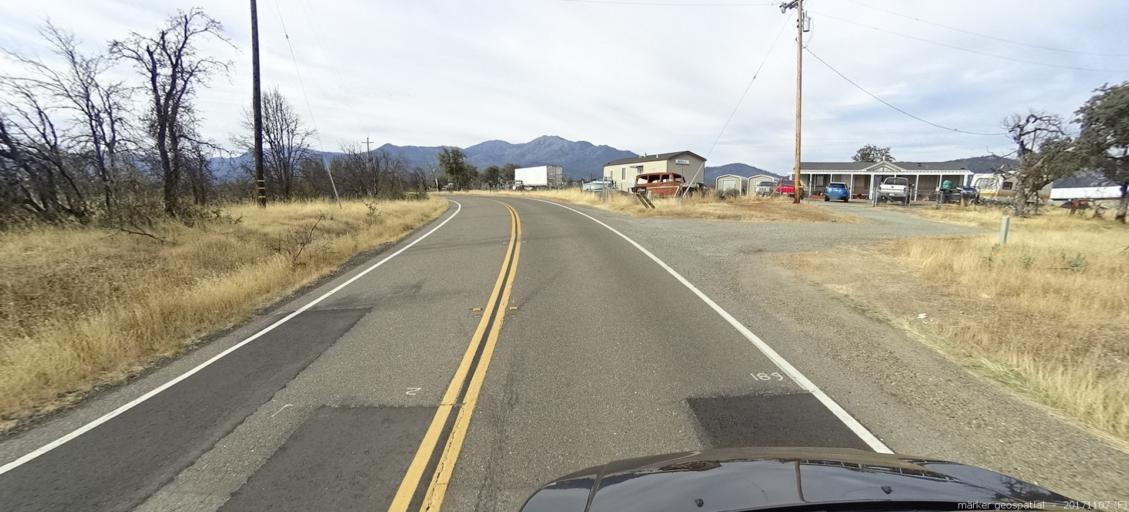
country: US
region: California
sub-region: Shasta County
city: Shasta
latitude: 40.4825
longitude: -122.5065
